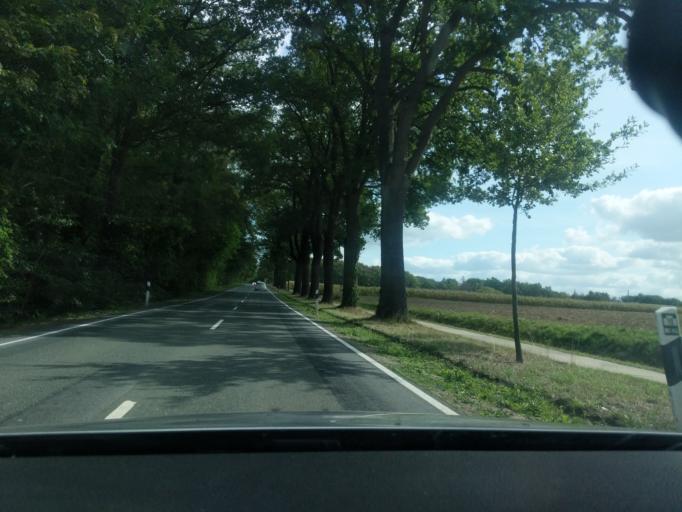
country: DE
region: Lower Saxony
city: Belm
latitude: 52.3090
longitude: 8.1000
